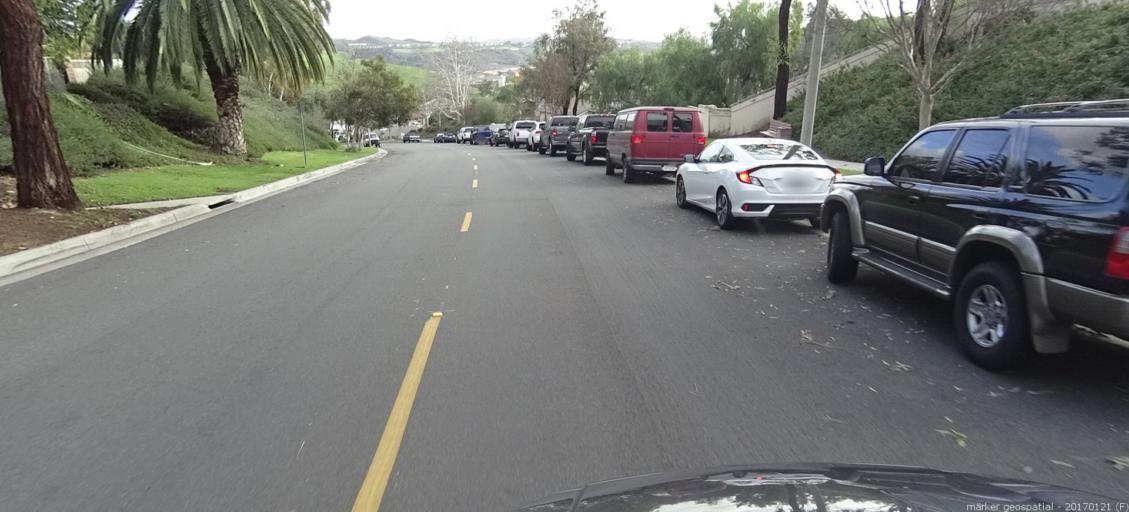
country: US
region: California
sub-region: Orange County
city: Portola Hills
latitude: 33.6857
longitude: -117.6274
